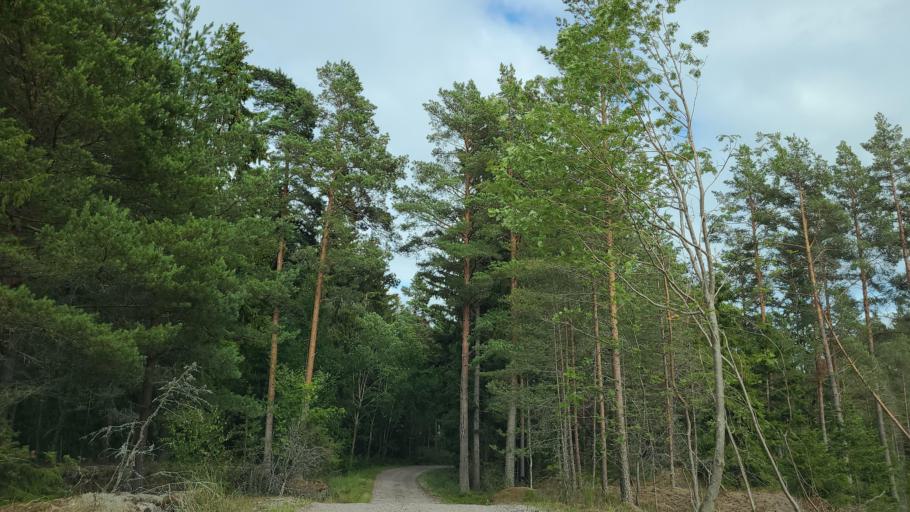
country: FI
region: Varsinais-Suomi
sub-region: Aboland-Turunmaa
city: Nagu
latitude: 60.1298
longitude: 21.8018
